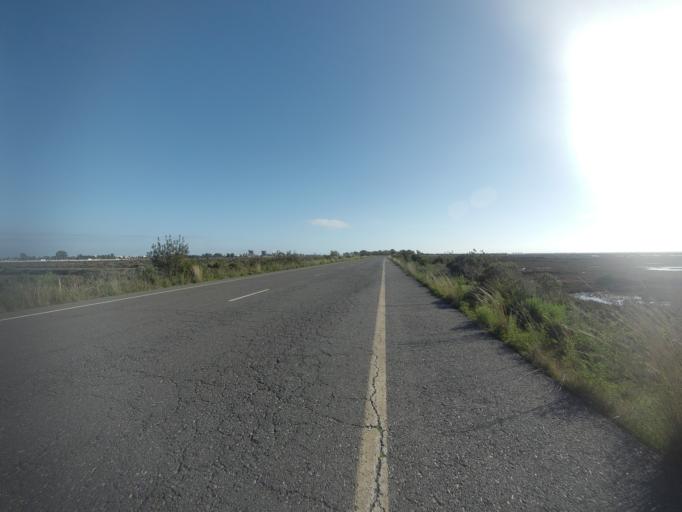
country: ES
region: Andalusia
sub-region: Provincia de Huelva
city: Huelva
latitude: 37.2457
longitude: -6.9663
